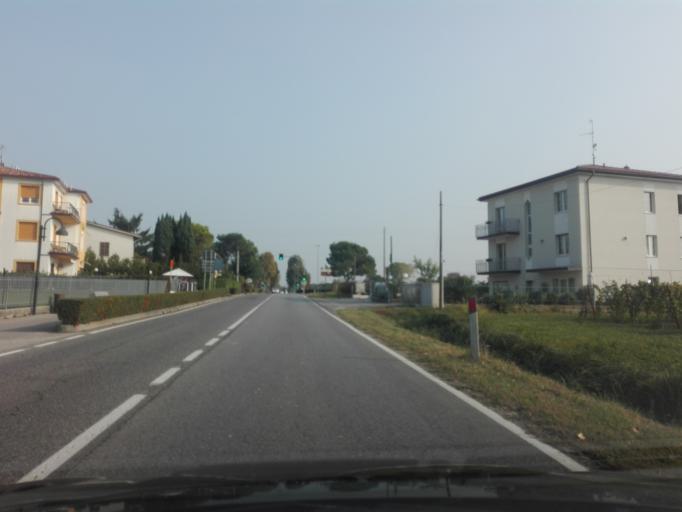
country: IT
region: Lombardy
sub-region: Provincia di Brescia
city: San Martino della Battaglia
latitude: 45.4583
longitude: 10.6342
